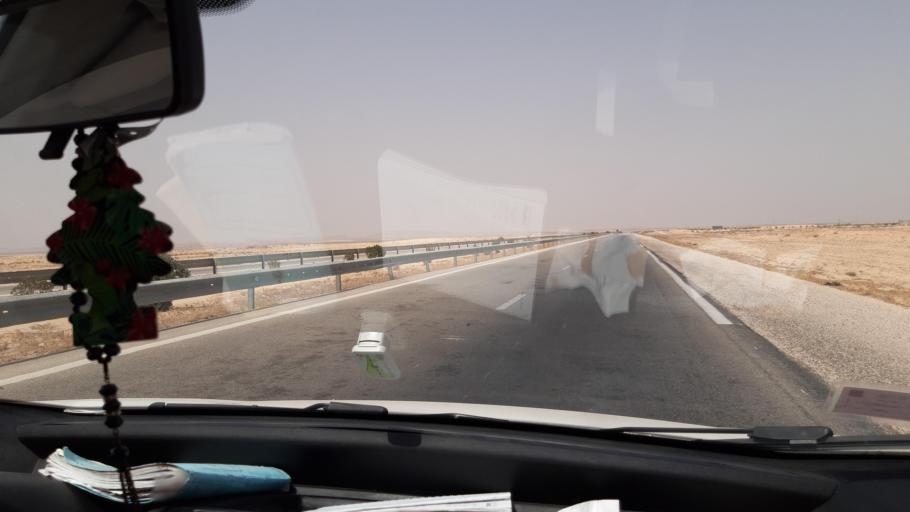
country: TN
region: Qabis
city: Gabes
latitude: 33.9463
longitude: 9.9594
